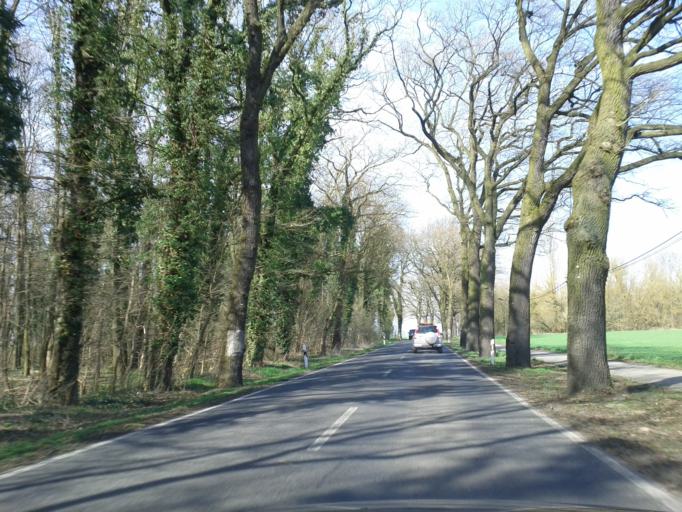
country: DE
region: Brandenburg
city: Schoneiche
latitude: 52.4870
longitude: 13.6943
